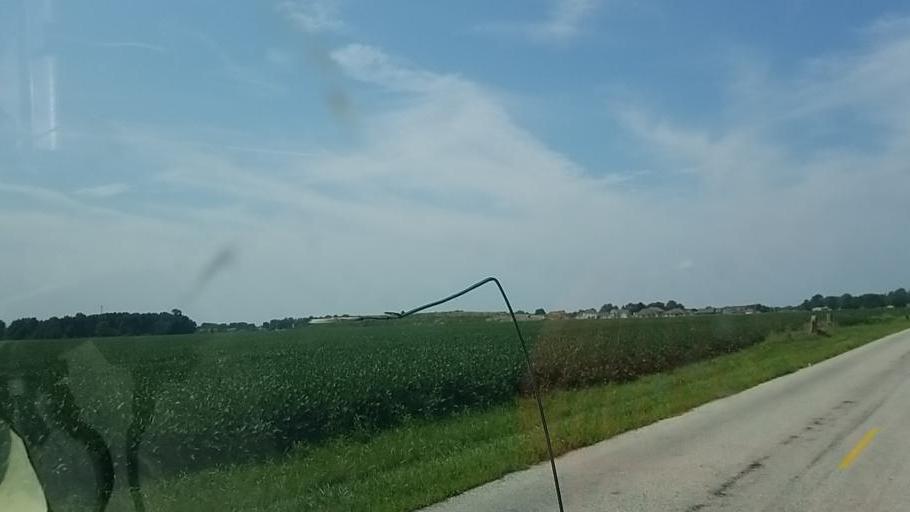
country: US
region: Ohio
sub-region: Marion County
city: Marion
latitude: 40.5978
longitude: -83.0633
